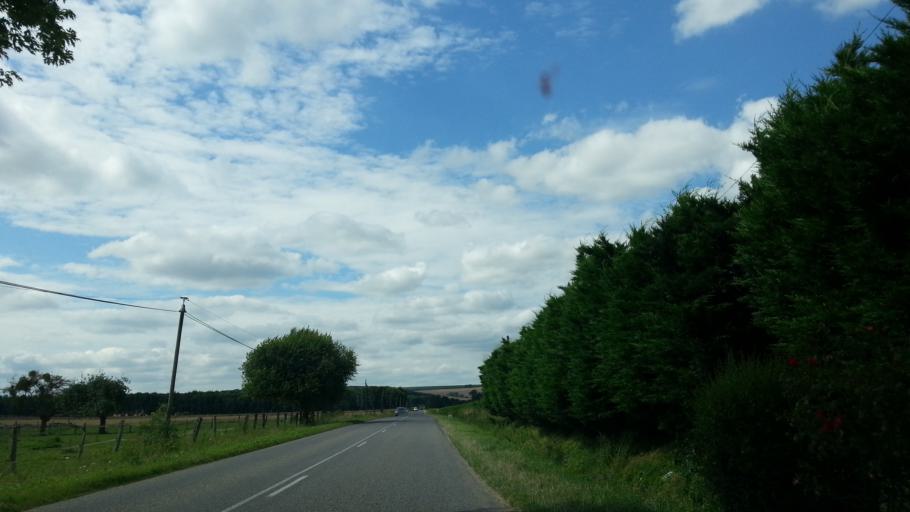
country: FR
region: Lorraine
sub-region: Departement de la Meuse
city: Thierville-sur-Meuse
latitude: 49.1753
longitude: 5.3462
